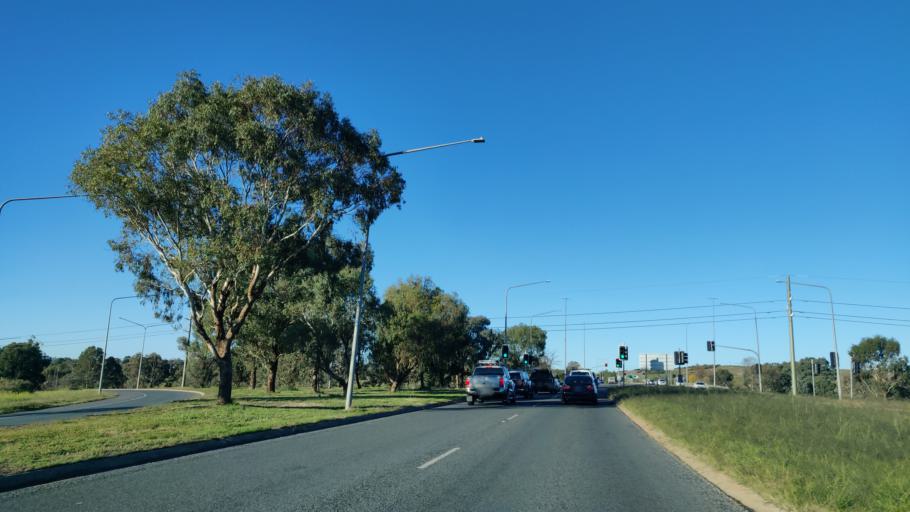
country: AU
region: Australian Capital Territory
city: Forrest
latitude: -35.3411
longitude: 149.1607
